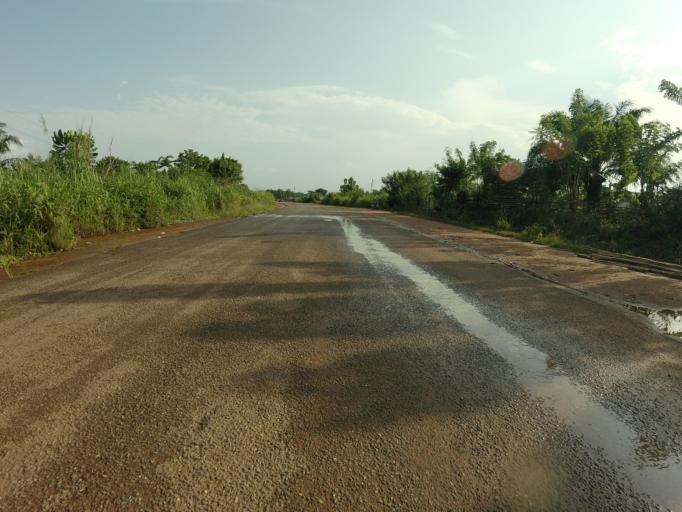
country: GH
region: Volta
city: Hohoe
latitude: 7.0784
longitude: 0.4393
